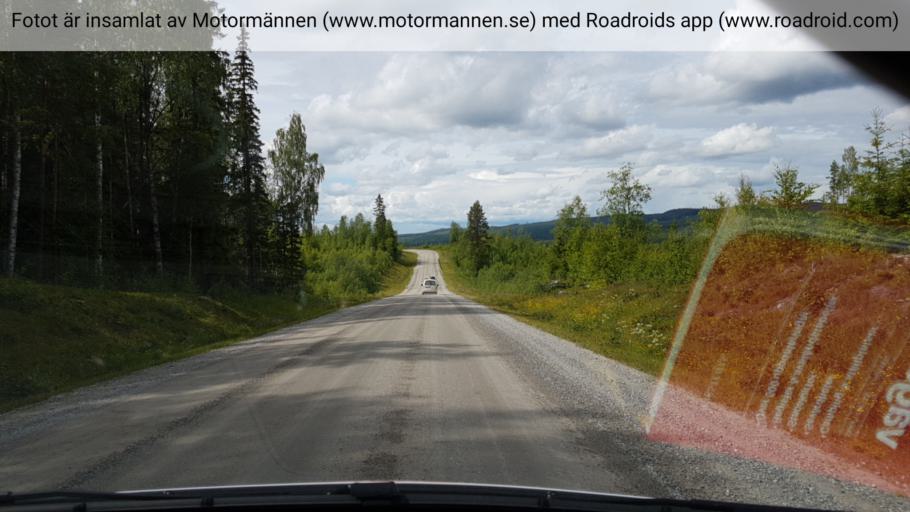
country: SE
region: Vaesternorrland
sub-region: Solleftea Kommun
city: Solleftea
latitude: 63.3167
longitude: 17.2432
